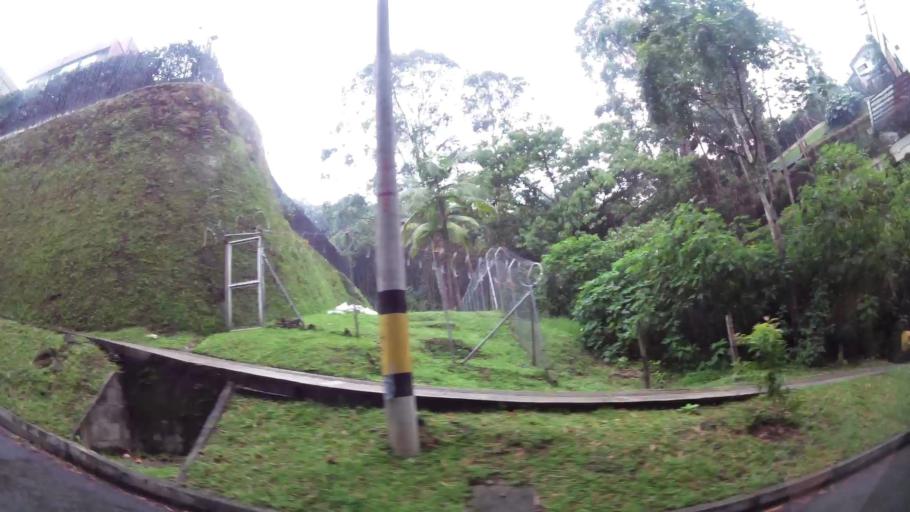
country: CO
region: Antioquia
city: Envigado
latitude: 6.1720
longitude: -75.5640
